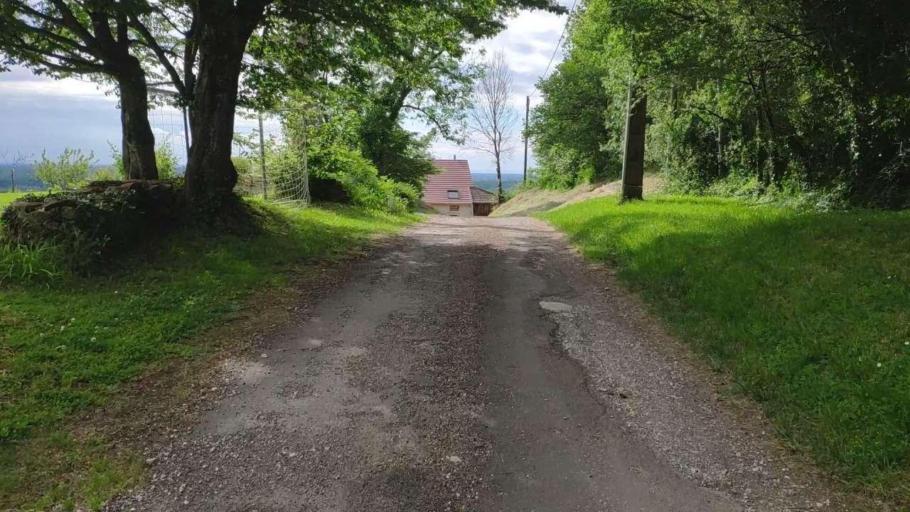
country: FR
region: Franche-Comte
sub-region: Departement du Jura
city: Bletterans
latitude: 46.7969
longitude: 5.5570
